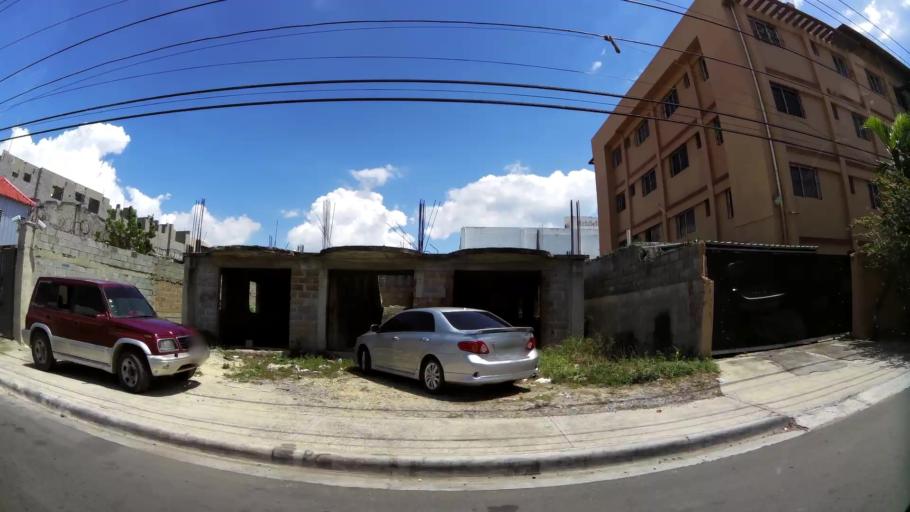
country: DO
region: Santo Domingo
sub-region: Santo Domingo
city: Santo Domingo Este
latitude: 18.4706
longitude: -69.8329
